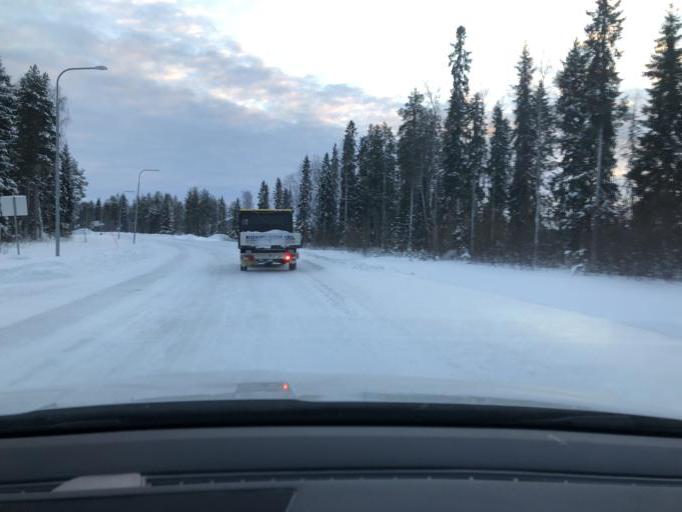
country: SE
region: Norrbotten
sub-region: Lulea Kommun
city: Bergnaset
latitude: 65.6208
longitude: 22.1162
